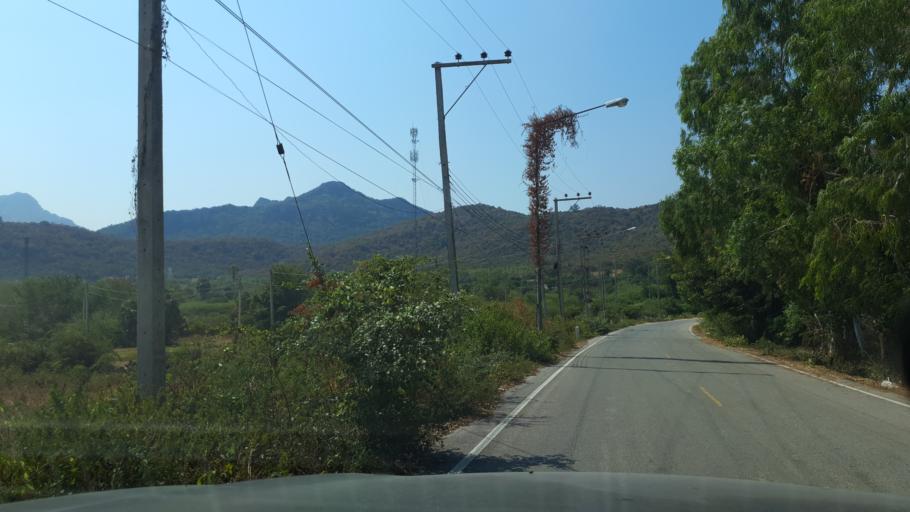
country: TH
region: Prachuap Khiri Khan
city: Sam Roi Yot
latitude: 12.2856
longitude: 99.9688
